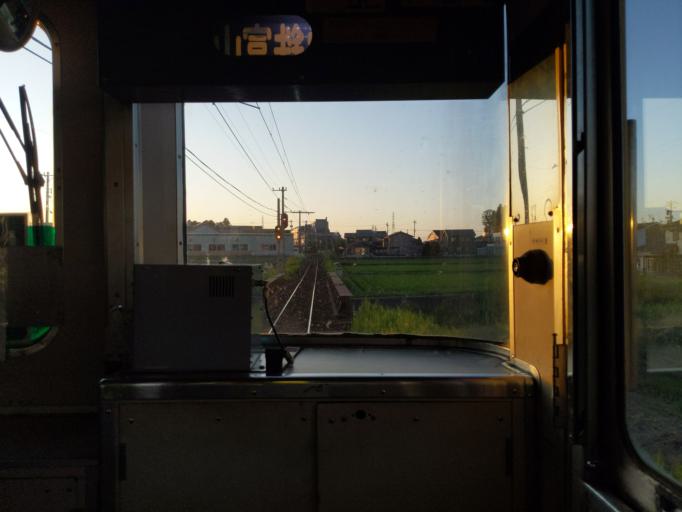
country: JP
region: Toyama
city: Kamiichi
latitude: 36.7044
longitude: 137.3093
